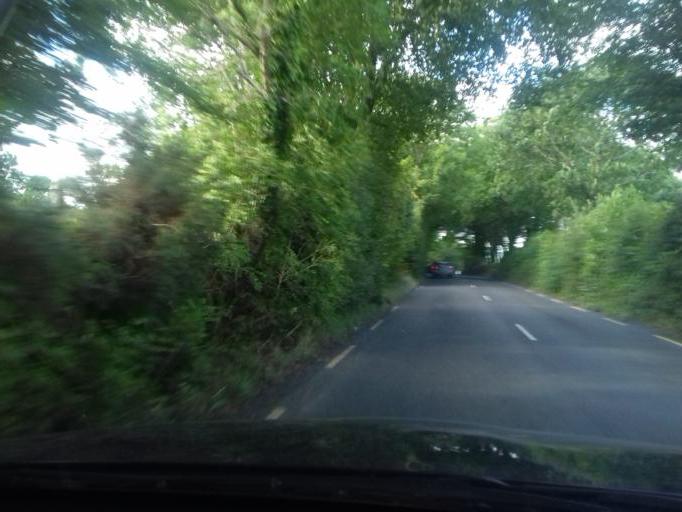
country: IE
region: Leinster
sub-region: Kilkenny
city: Graiguenamanagh
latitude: 52.4748
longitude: -6.9526
